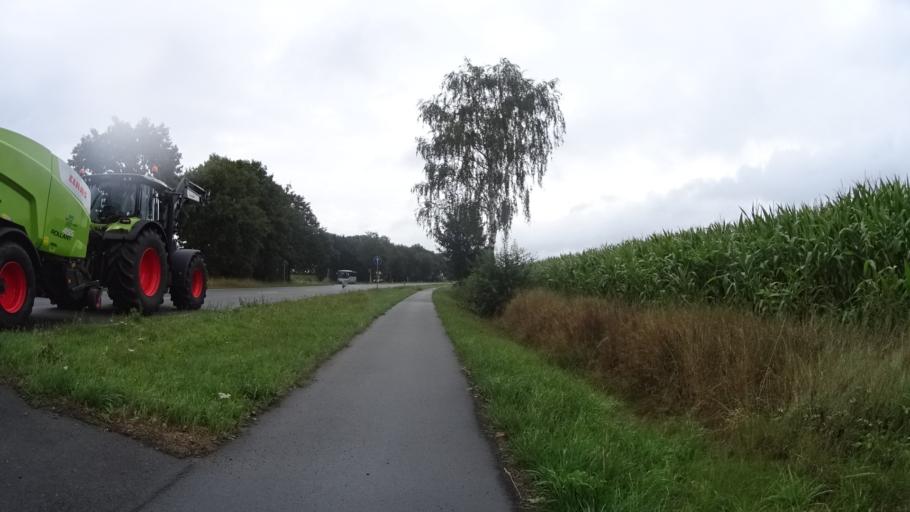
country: DE
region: Lower Saxony
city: Brinkum
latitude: 53.2756
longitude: 7.5639
